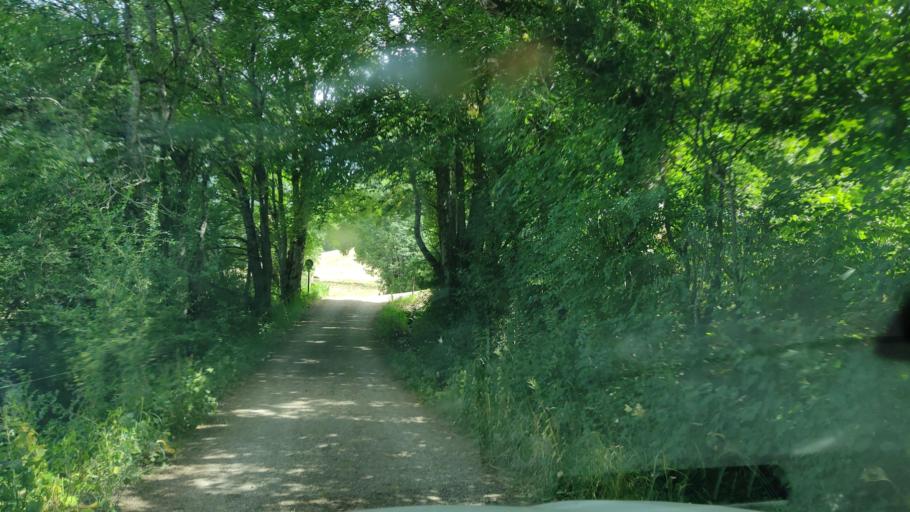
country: FR
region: Rhone-Alpes
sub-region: Departement de la Savoie
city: Cruet
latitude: 45.6085
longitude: 6.1129
